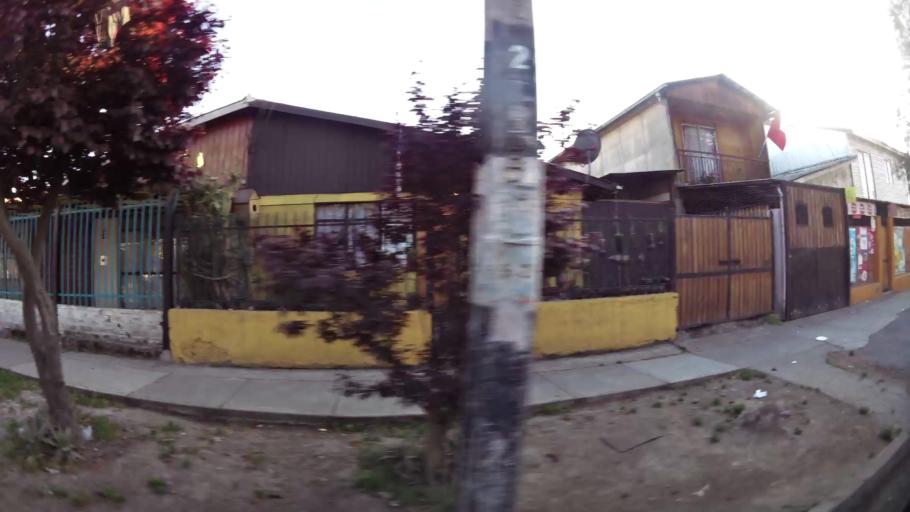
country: CL
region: Santiago Metropolitan
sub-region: Provincia de Santiago
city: Santiago
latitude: -33.3768
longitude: -70.6342
